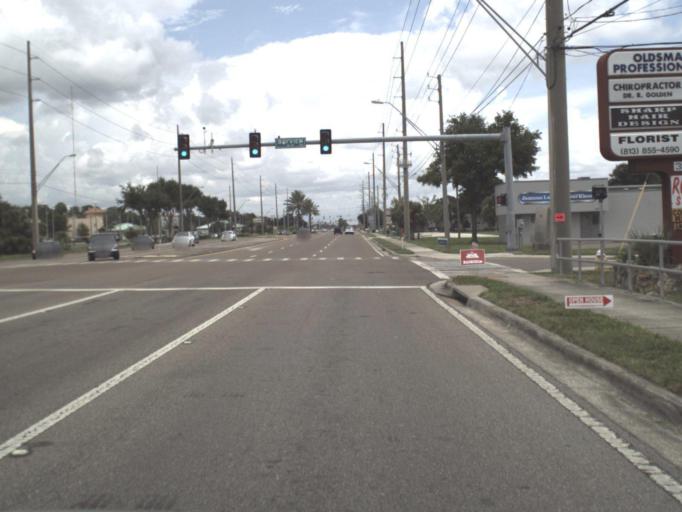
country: US
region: Florida
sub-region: Pinellas County
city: Oldsmar
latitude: 28.0403
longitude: -82.6685
